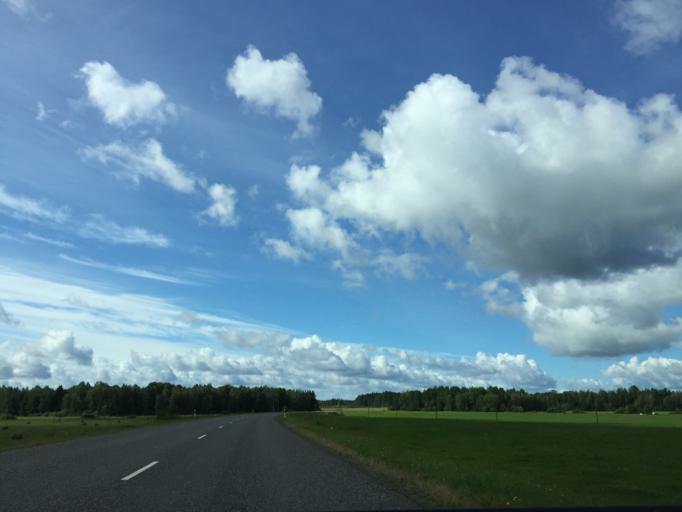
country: LV
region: Kuldigas Rajons
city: Kuldiga
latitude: 56.9979
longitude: 22.1278
